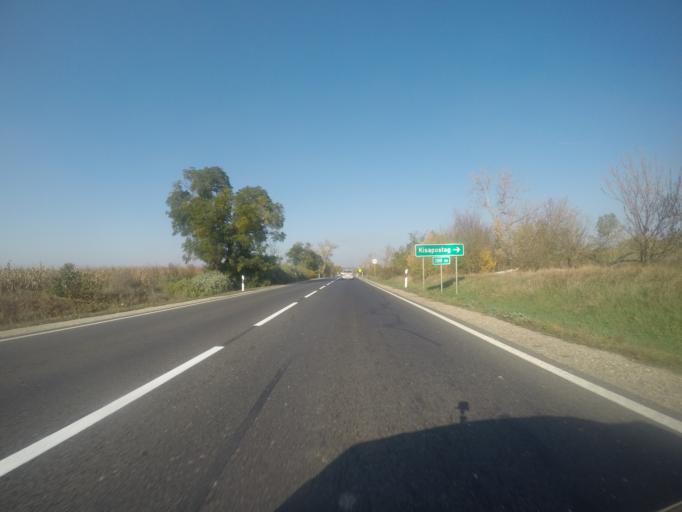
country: HU
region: Fejer
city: Baracs
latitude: 46.8979
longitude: 18.9227
